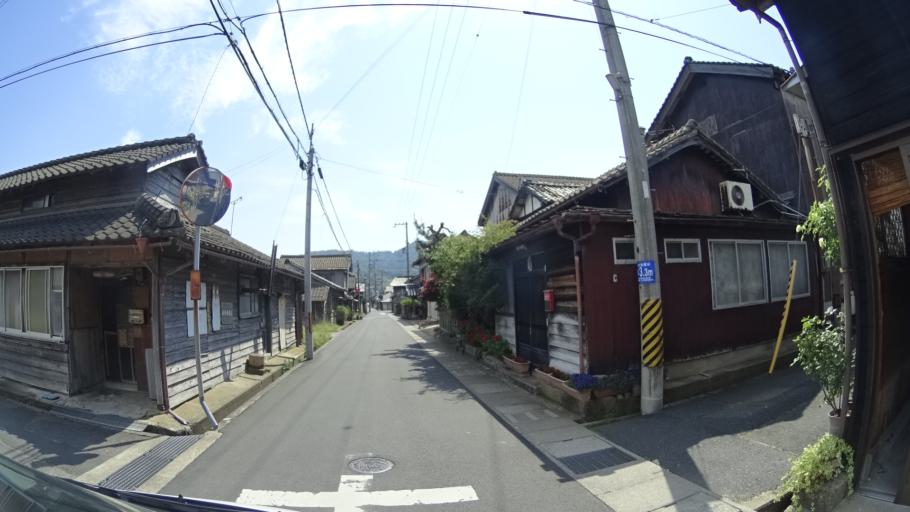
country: JP
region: Kyoto
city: Miyazu
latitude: 35.6851
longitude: 135.0254
